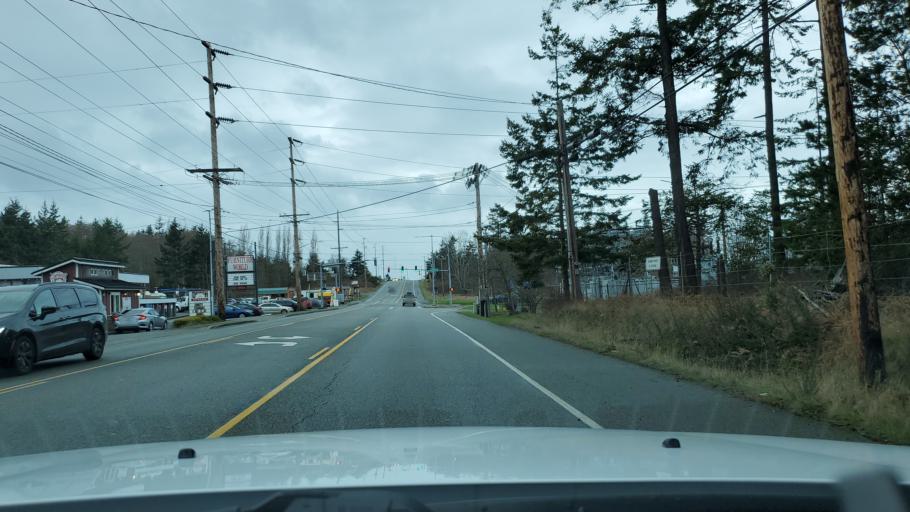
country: US
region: Washington
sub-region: Island County
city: Ault Field
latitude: 48.3259
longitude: -122.6680
